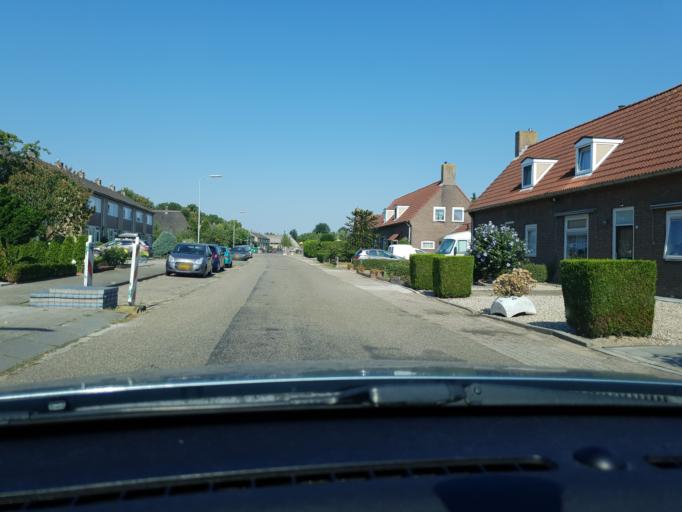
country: NL
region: Gelderland
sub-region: Gemeente Nijmegen
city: Lindenholt
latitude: 51.8531
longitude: 5.8122
